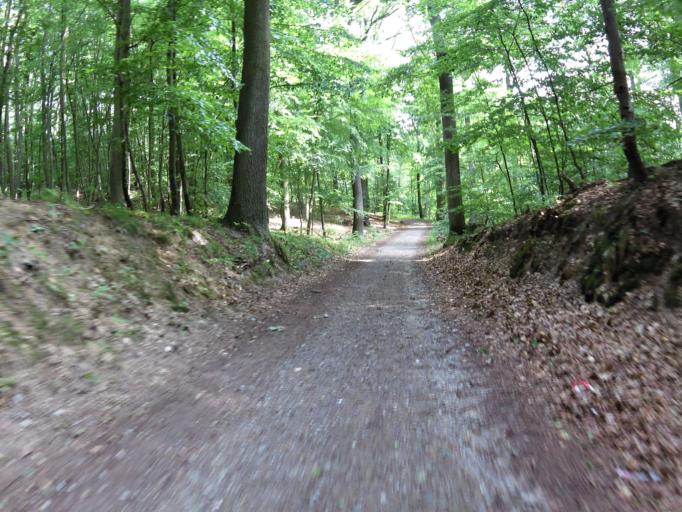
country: DE
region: Mecklenburg-Vorpommern
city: Seebad Bansin
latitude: 53.9570
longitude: 14.1069
